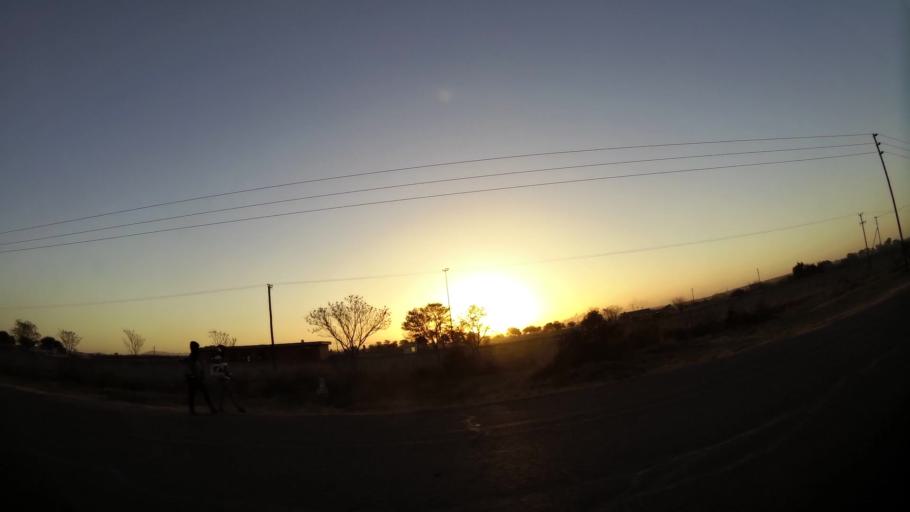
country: ZA
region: North-West
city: Ga-Rankuwa
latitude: -25.5767
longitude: 28.0496
